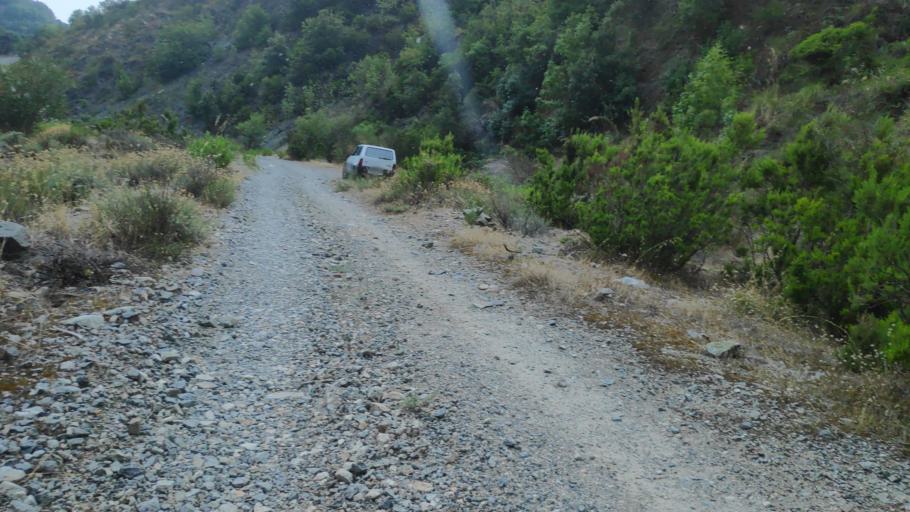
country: IT
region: Calabria
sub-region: Provincia di Reggio Calabria
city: Bivongi
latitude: 38.4930
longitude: 16.4504
